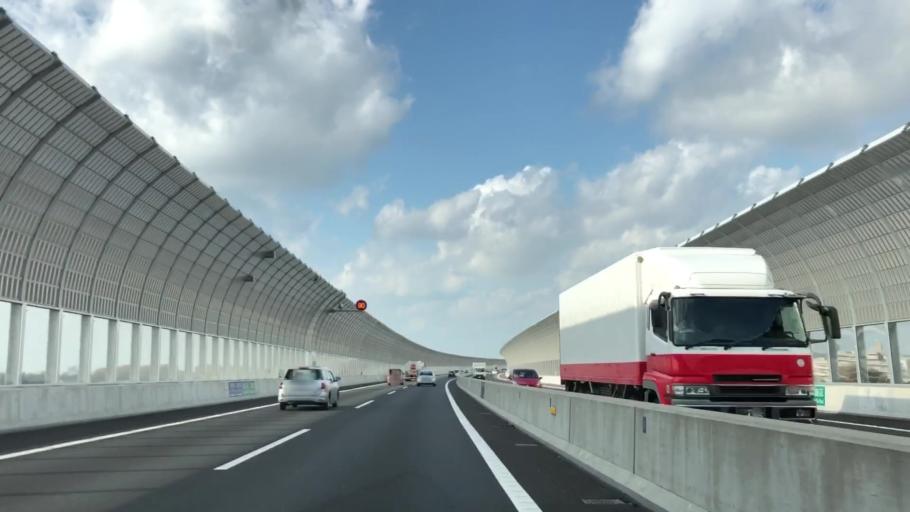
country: JP
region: Chiba
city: Matsudo
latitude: 35.7827
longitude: 139.8836
